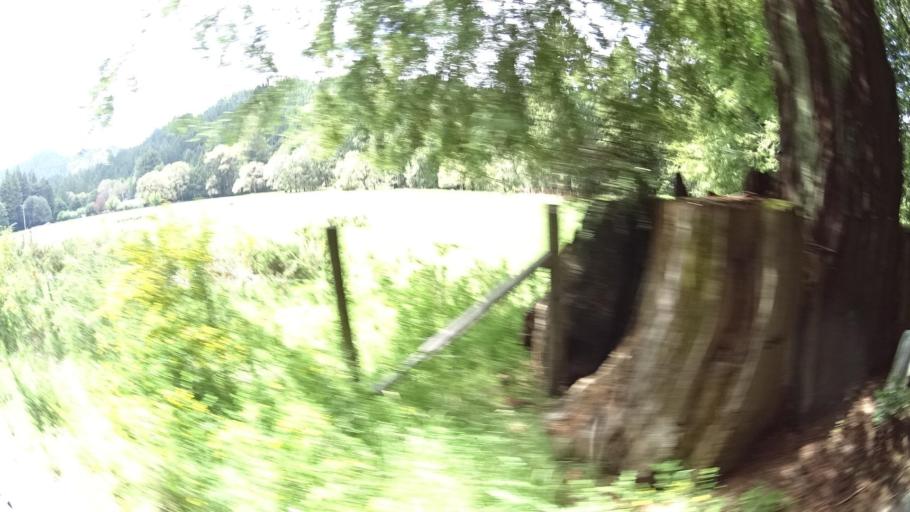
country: US
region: California
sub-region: Humboldt County
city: Redway
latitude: 40.0302
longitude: -123.9499
